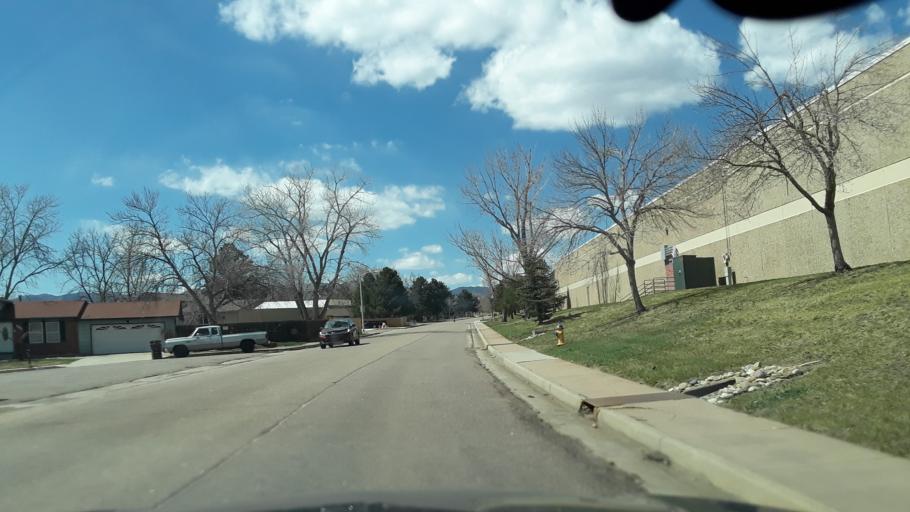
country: US
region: Colorado
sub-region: El Paso County
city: Colorado Springs
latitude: 38.9042
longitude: -104.7806
